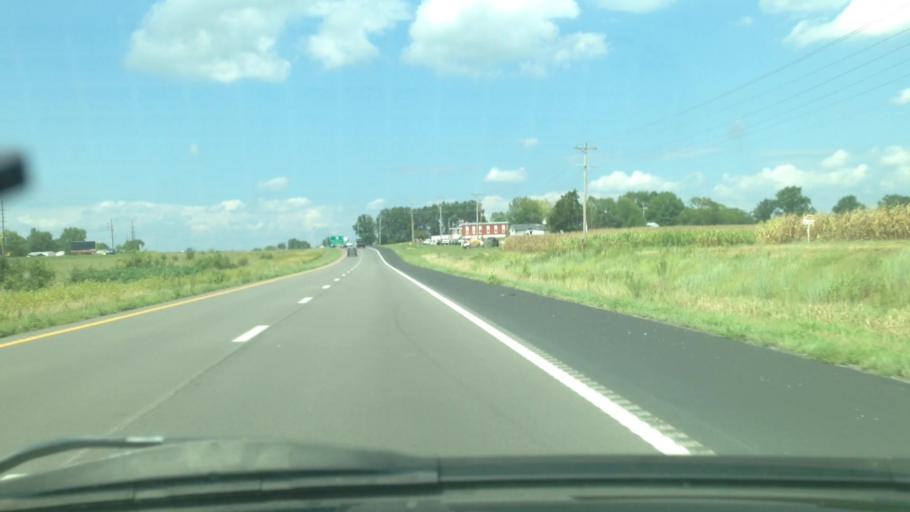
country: US
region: Missouri
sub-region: Lincoln County
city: Moscow Mills
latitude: 38.9368
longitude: -90.9254
